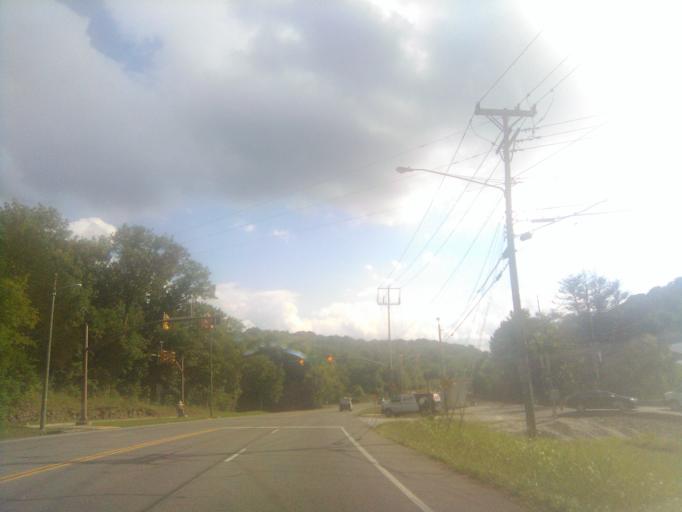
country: US
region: Tennessee
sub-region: Davidson County
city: Belle Meade
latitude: 36.0792
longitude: -86.8850
